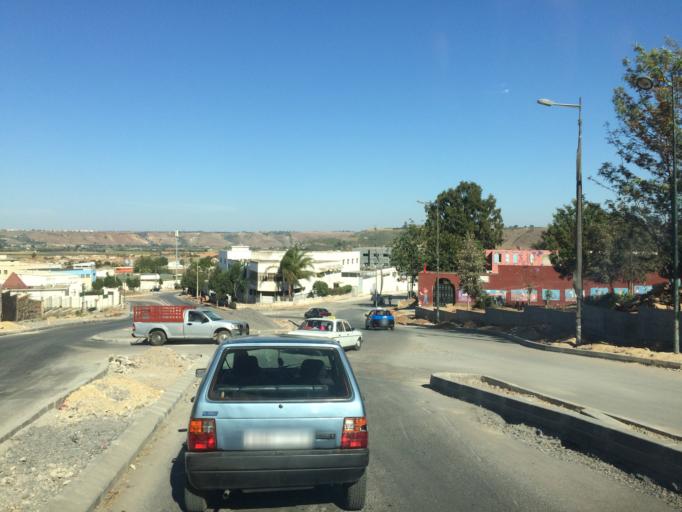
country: MA
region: Rabat-Sale-Zemmour-Zaer
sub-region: Rabat
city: Rabat
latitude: 33.9909
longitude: -6.8091
